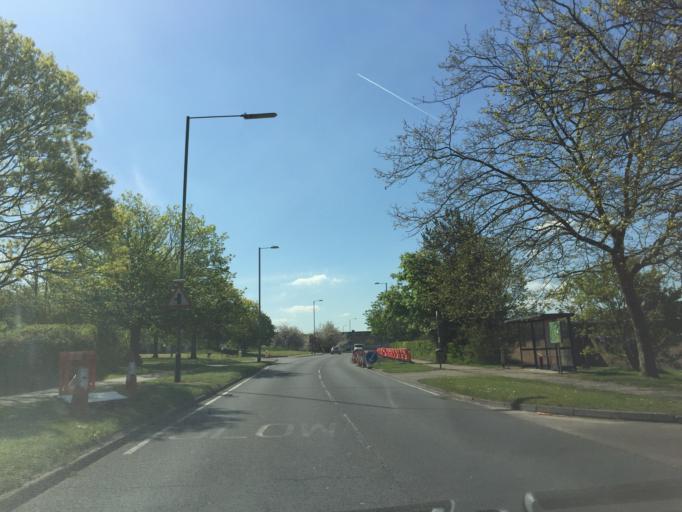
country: GB
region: England
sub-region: Essex
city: Harlow
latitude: 51.7559
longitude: 0.0907
